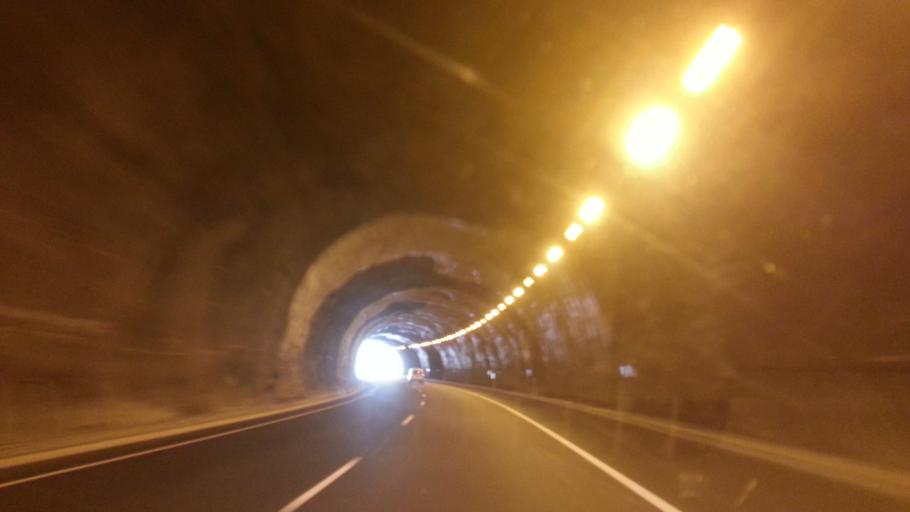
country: ES
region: Catalonia
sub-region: Provincia de Barcelona
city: Sant Pere de Ribes
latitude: 41.2999
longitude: 1.7271
